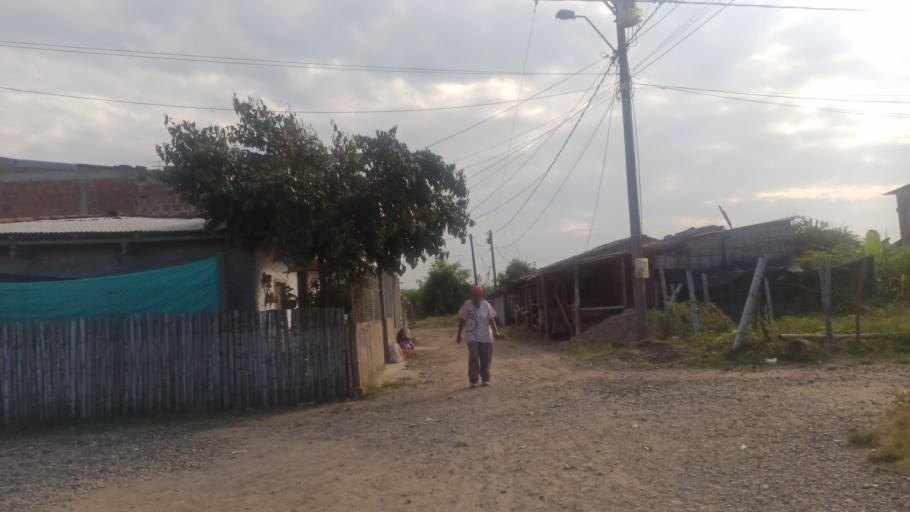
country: CO
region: Valle del Cauca
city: Jamundi
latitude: 3.1303
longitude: -76.5582
